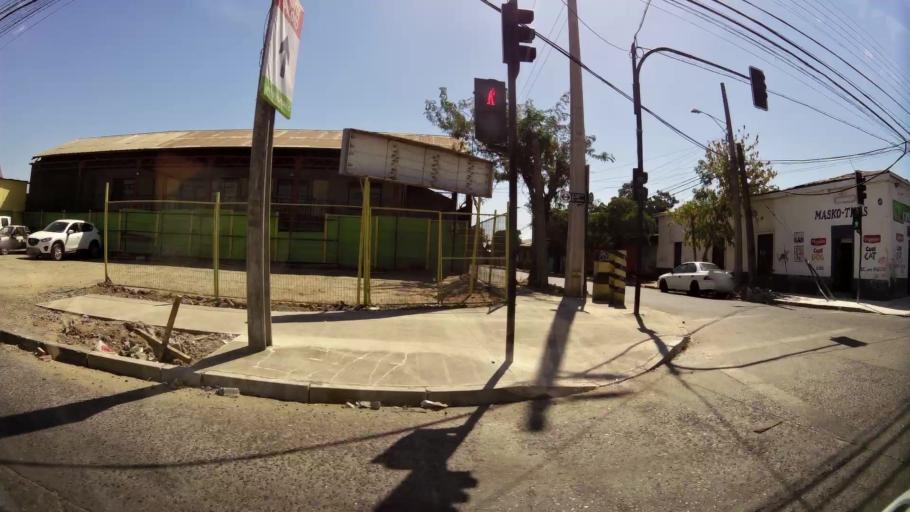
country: CL
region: Maule
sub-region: Provincia de Talca
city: Talca
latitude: -35.4365
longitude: -71.6513
